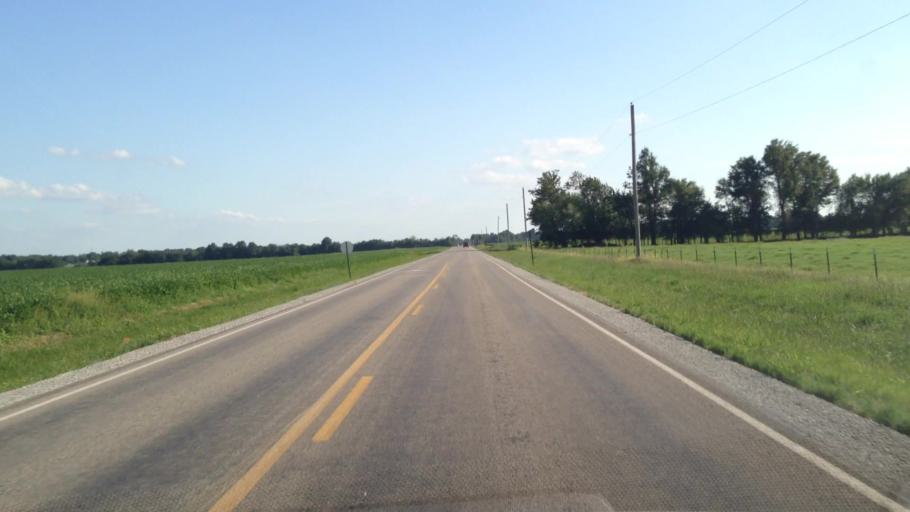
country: US
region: Kansas
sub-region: Crawford County
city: Pittsburg
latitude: 37.3622
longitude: -94.6315
